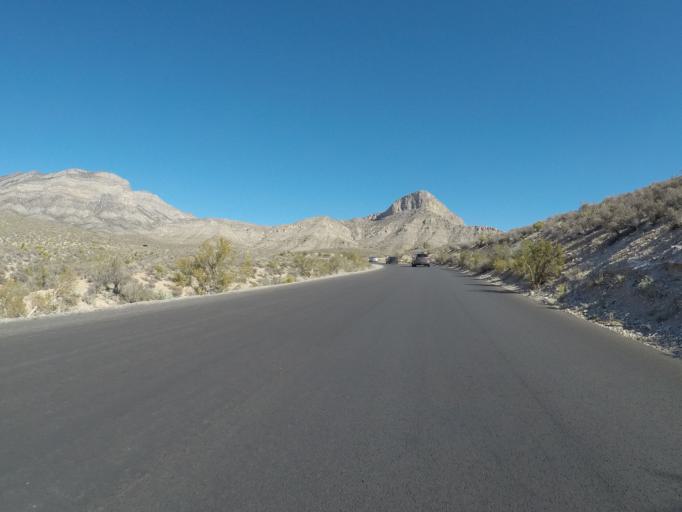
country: US
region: Nevada
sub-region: Clark County
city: Summerlin South
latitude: 36.1662
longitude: -115.4625
